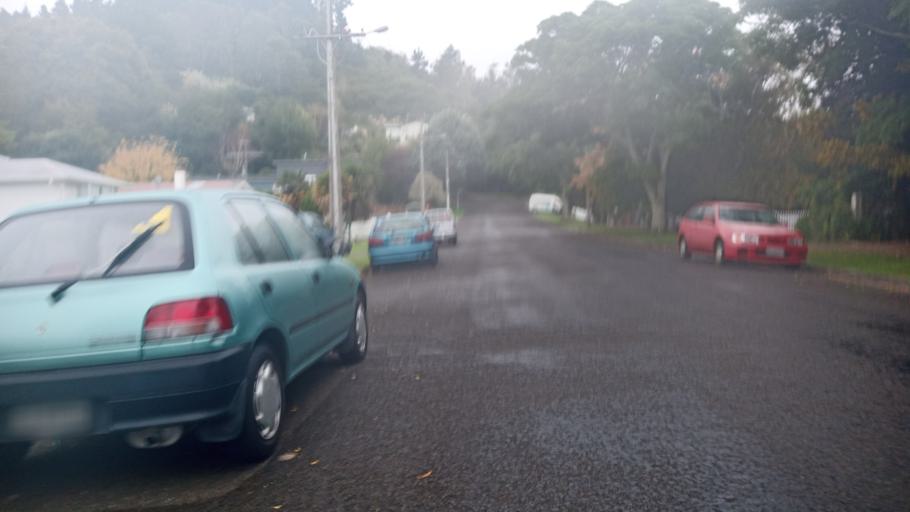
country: NZ
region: Gisborne
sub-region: Gisborne District
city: Gisborne
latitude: -38.6542
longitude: 178.0323
